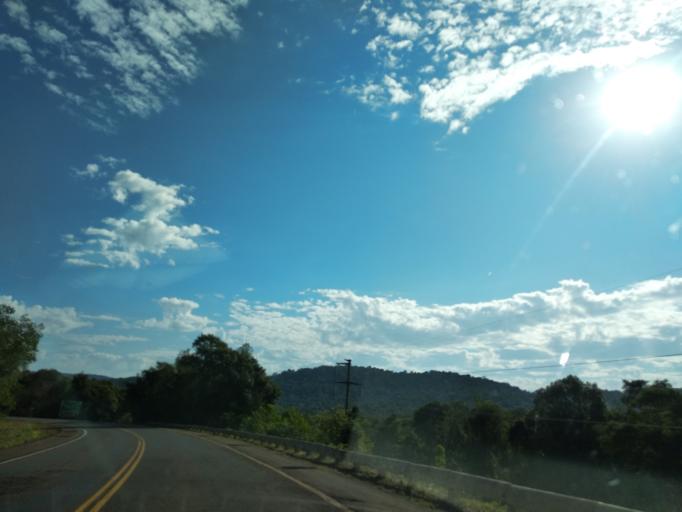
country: AR
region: Misiones
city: Aristobulo del Valle
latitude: -27.0918
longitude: -54.9484
